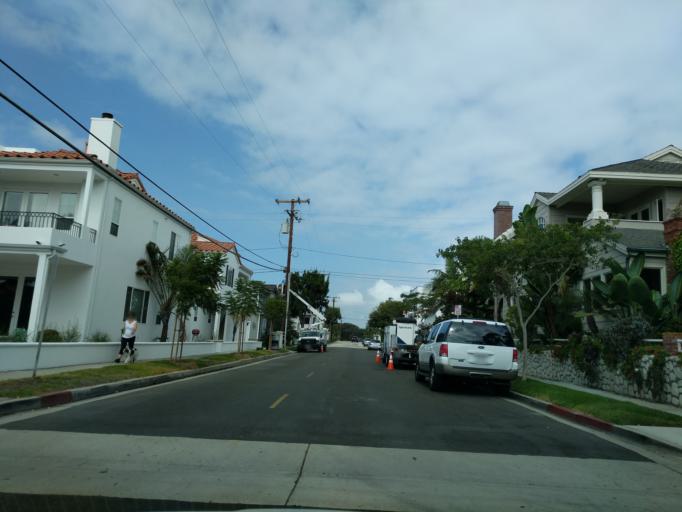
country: US
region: California
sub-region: Orange County
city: San Joaquin Hills
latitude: 33.5933
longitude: -117.8700
